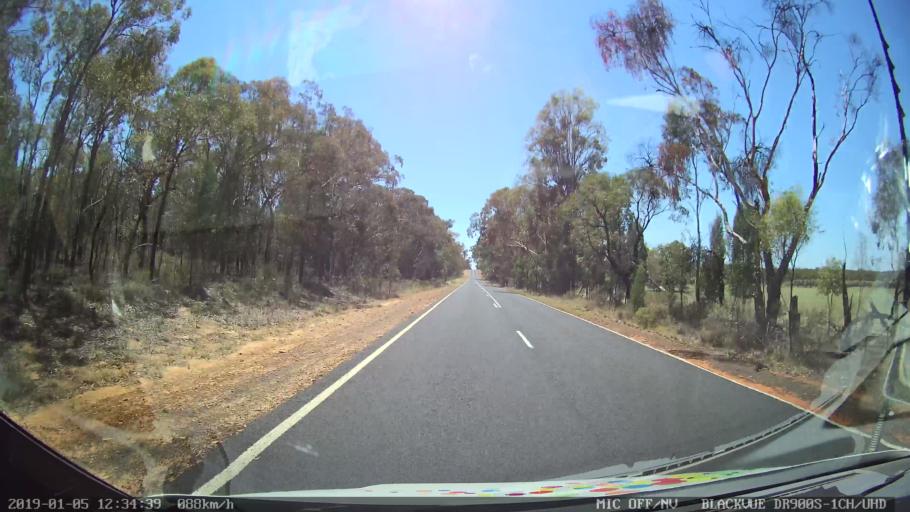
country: AU
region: New South Wales
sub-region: Warrumbungle Shire
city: Coonabarabran
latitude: -31.2116
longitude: 149.4136
